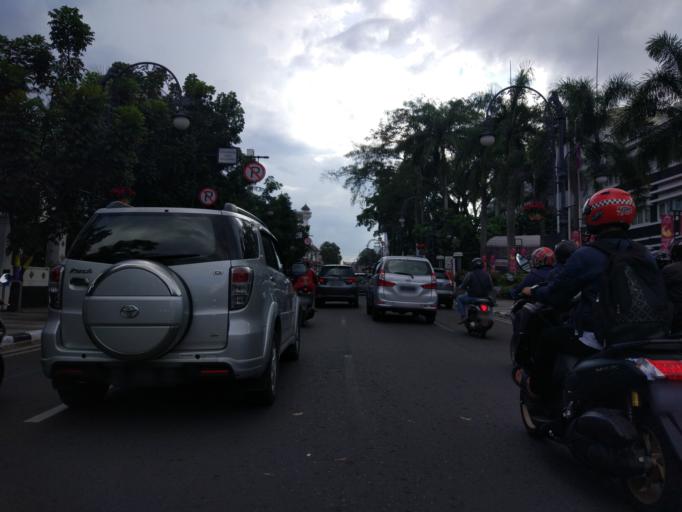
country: ID
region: West Java
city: Bandung
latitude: -6.9218
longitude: 107.6119
